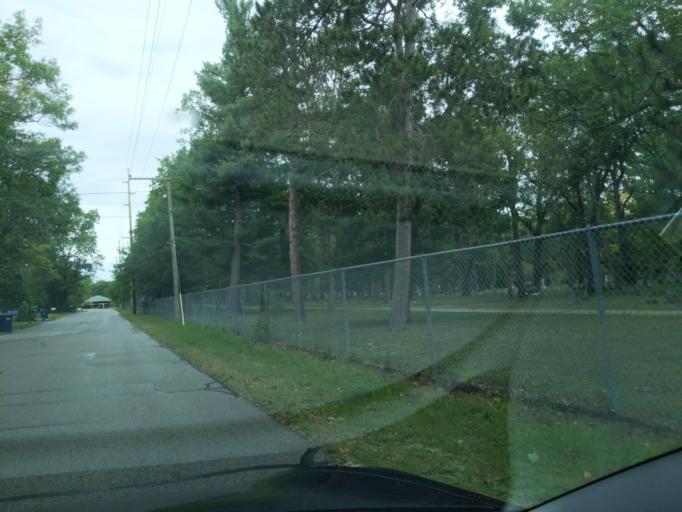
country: US
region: Michigan
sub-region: Grand Traverse County
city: Traverse City
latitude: 44.7561
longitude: -85.5903
